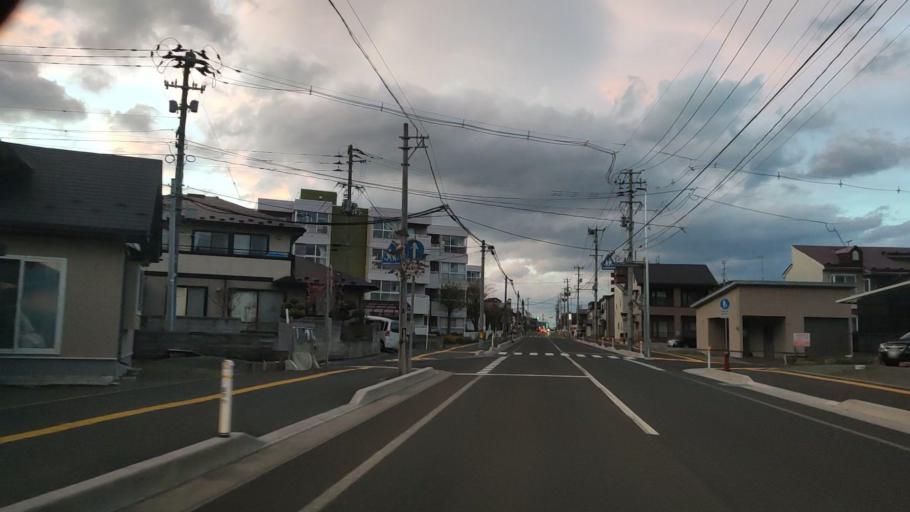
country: JP
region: Iwate
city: Morioka-shi
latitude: 39.7197
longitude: 141.1086
